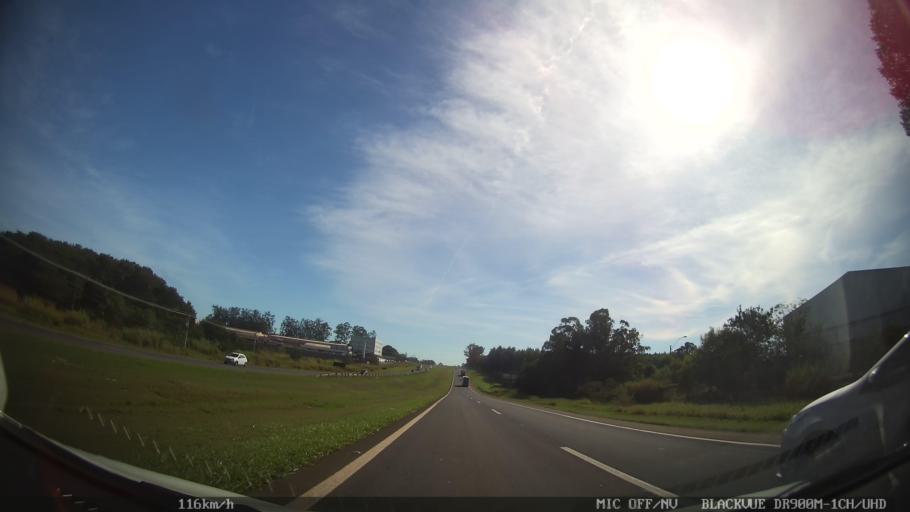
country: BR
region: Sao Paulo
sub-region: Leme
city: Leme
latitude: -22.2101
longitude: -47.3941
